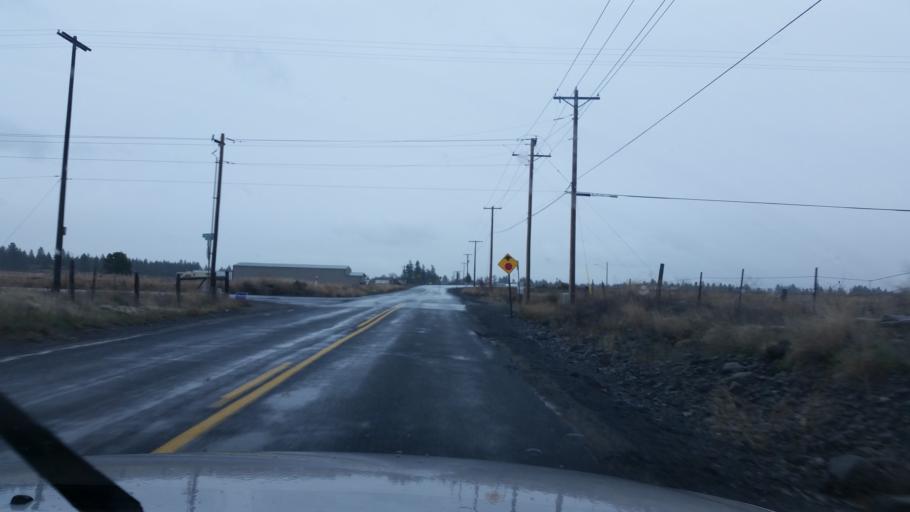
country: US
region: Washington
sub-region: Spokane County
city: Airway Heights
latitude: 47.6719
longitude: -117.5618
